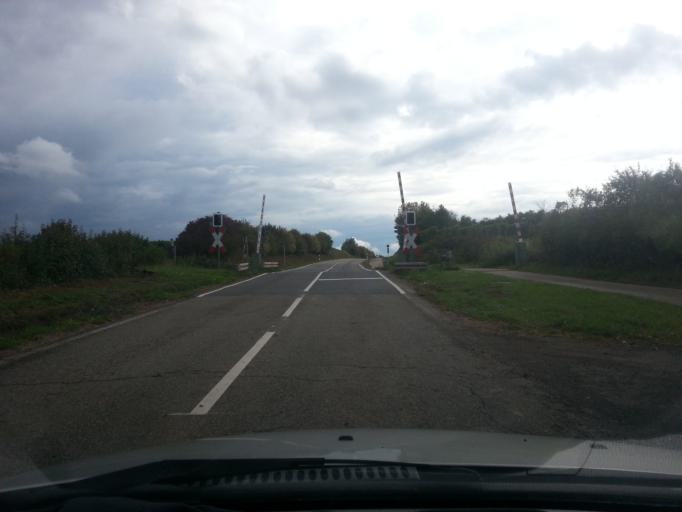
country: DE
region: Rheinland-Pfalz
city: Freinsheim
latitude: 49.5016
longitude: 8.2213
